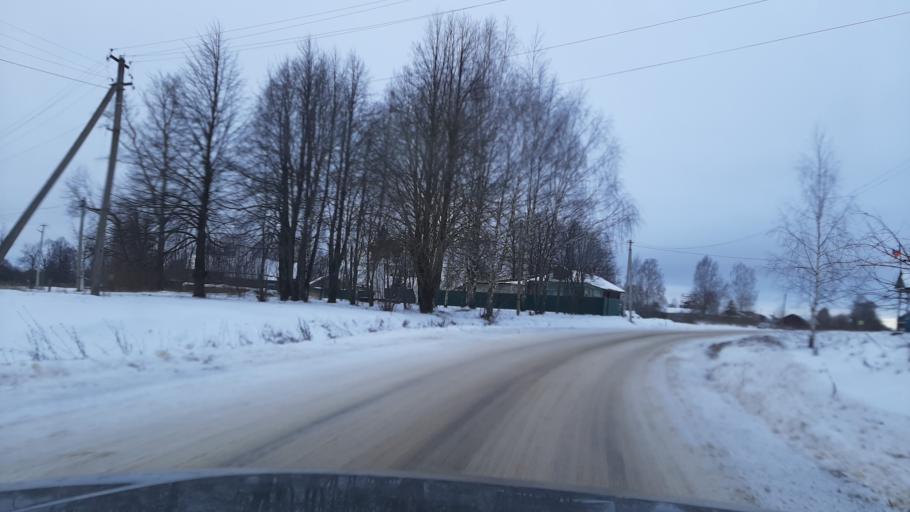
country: RU
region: Kostroma
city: Volgorechensk
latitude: 57.4341
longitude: 41.0695
